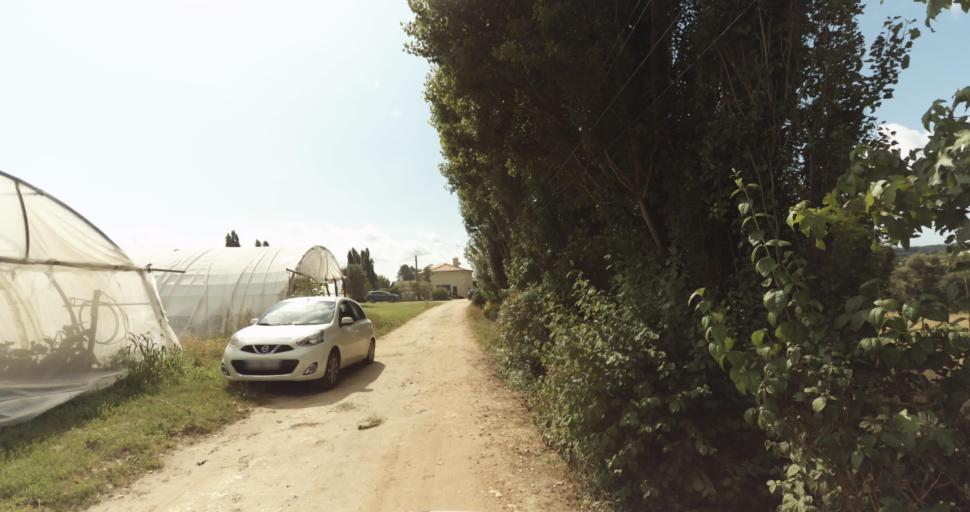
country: FR
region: Aquitaine
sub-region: Departement de la Gironde
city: Bazas
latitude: 44.4379
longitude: -0.1938
